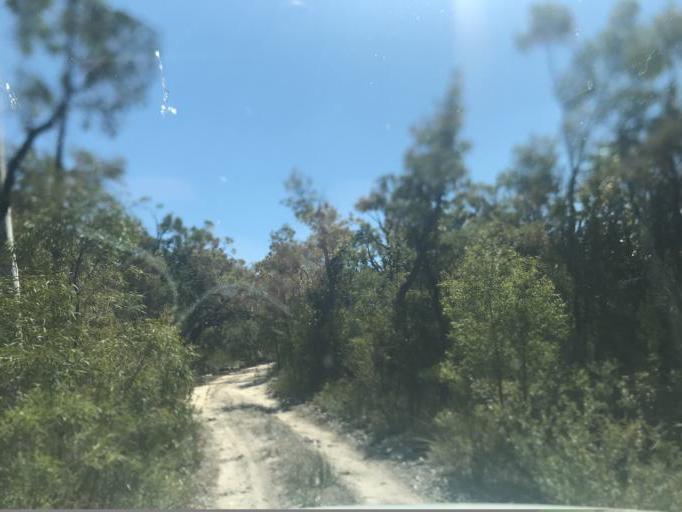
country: AU
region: New South Wales
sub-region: Wyong Shire
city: Little Jilliby
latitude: -33.1524
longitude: 151.1003
